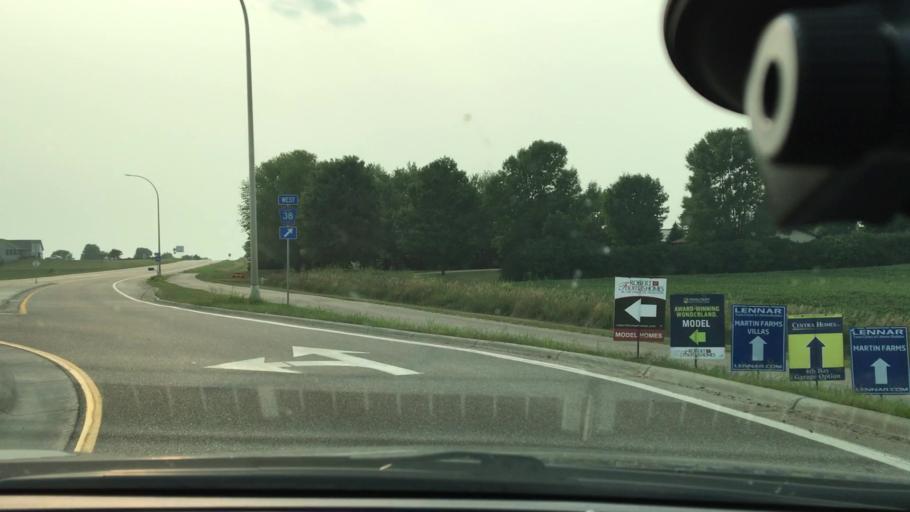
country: US
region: Minnesota
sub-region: Wright County
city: Otsego
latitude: 45.2526
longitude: -93.6006
